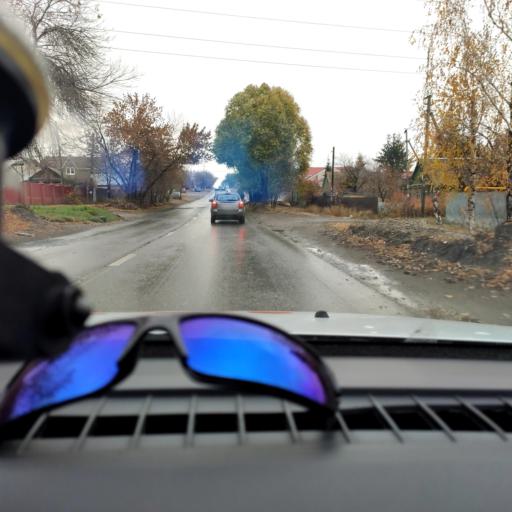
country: RU
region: Samara
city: Samara
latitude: 53.1761
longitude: 50.1810
